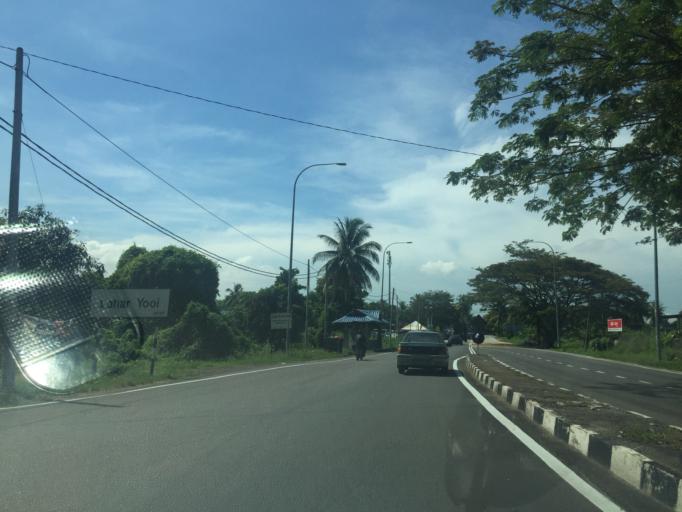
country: MY
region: Penang
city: Tasek Glugor
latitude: 5.4695
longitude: 100.4571
